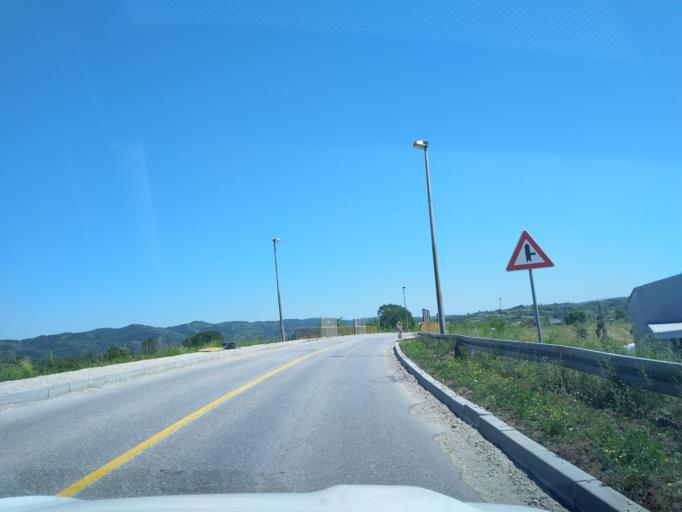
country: RS
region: Central Serbia
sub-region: Zlatiborski Okrug
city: Pozega
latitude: 43.8349
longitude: 20.0432
